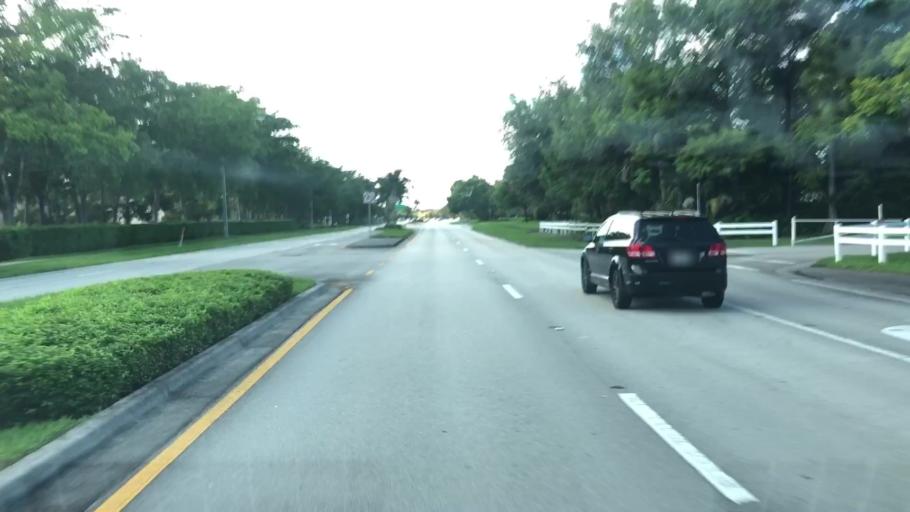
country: US
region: Florida
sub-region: Broward County
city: Coral Springs
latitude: 26.2453
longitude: -80.2690
